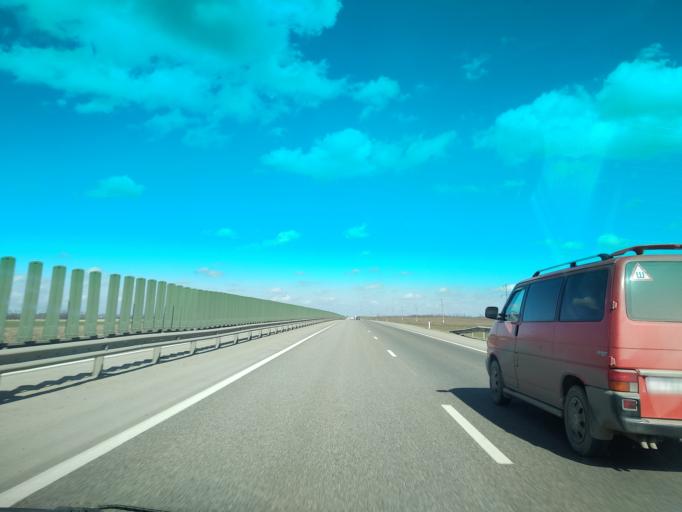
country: RU
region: Krasnodarskiy
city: Dinskaya
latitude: 45.2620
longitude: 39.2062
